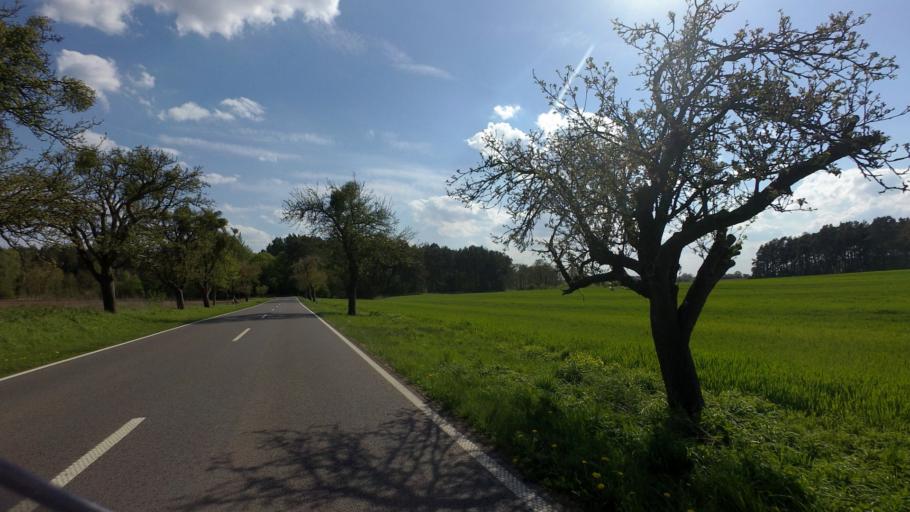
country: DE
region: Brandenburg
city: Templin
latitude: 53.0998
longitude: 13.5005
